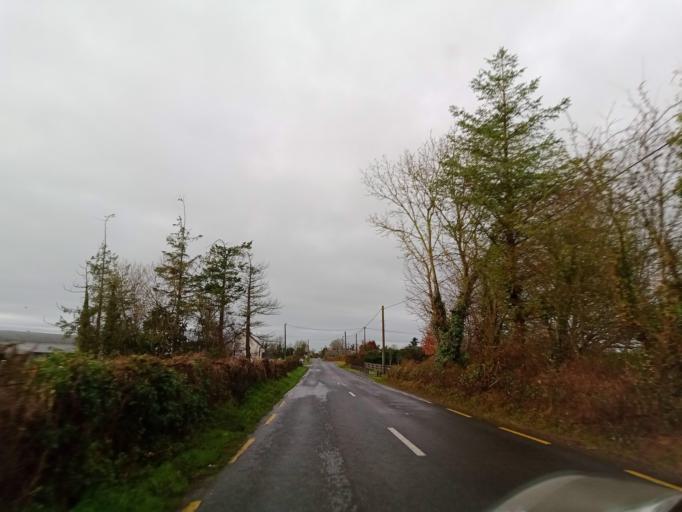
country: IE
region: Leinster
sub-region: Kilkenny
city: Callan
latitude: 52.5696
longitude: -7.4272
